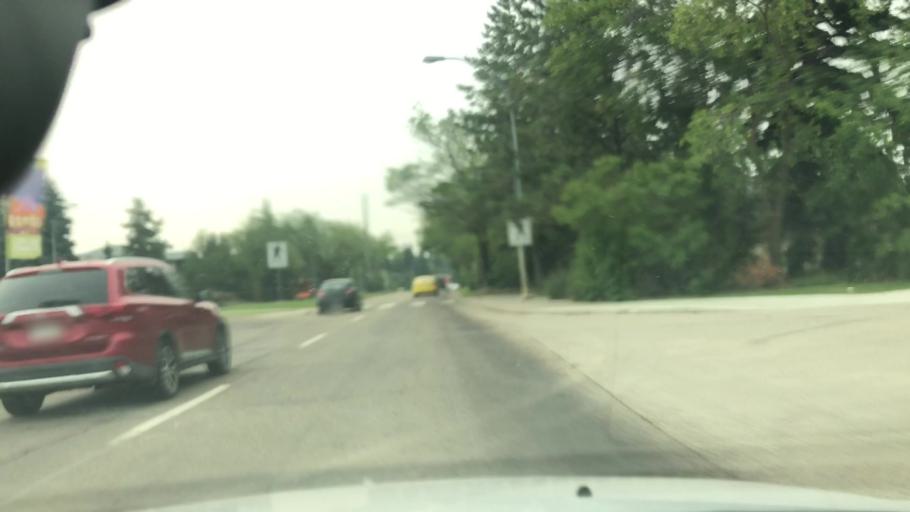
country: CA
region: Alberta
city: Edmonton
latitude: 53.5228
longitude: -113.5409
